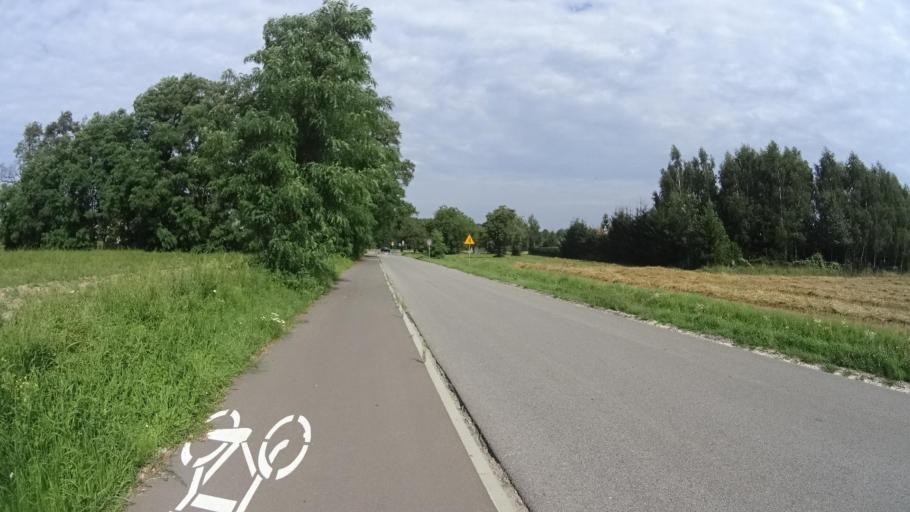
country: PL
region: Masovian Voivodeship
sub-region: Powiat piaseczynski
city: Tarczyn
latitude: 52.0216
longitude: 20.7878
